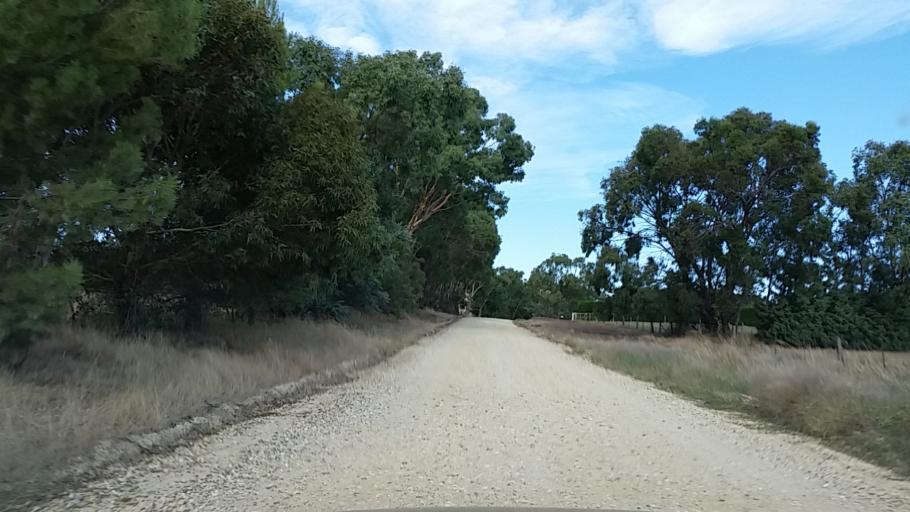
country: AU
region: South Australia
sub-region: Barossa
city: Angaston
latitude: -34.5590
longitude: 139.0929
